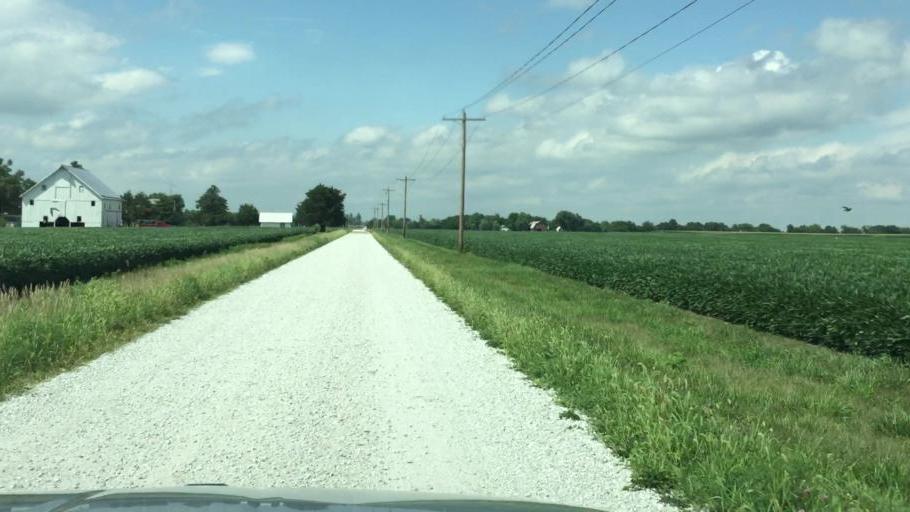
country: US
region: Illinois
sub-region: Hancock County
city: Carthage
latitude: 40.5317
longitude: -91.1575
